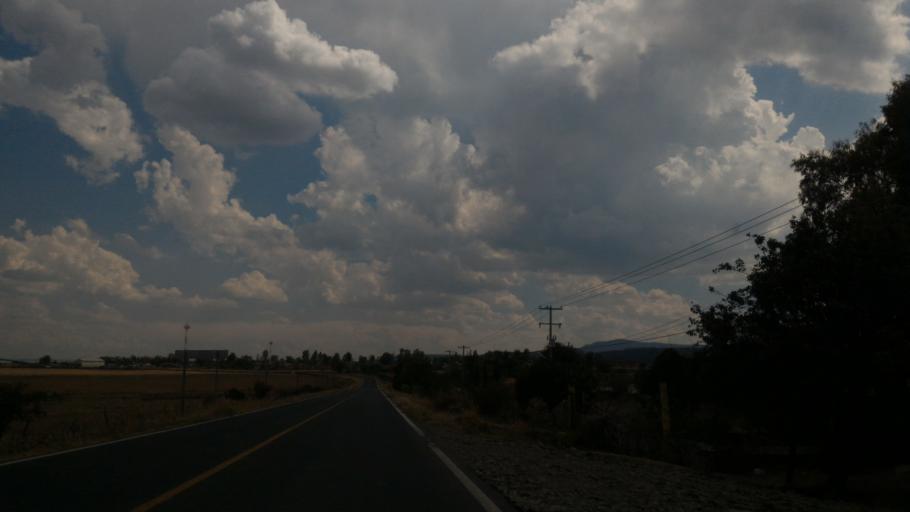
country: MX
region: Guanajuato
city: Ciudad Manuel Doblado
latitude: 20.8104
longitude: -101.9979
